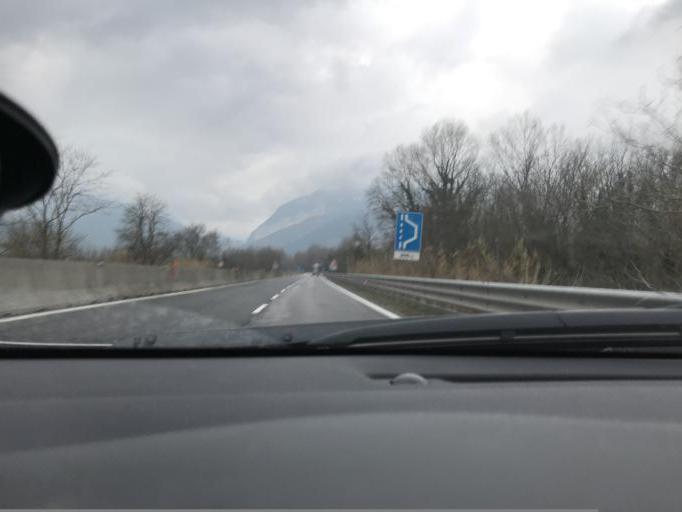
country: IT
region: The Marches
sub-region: Provincia di Ancona
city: Serra San Quirico
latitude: 43.4513
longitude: 13.0417
